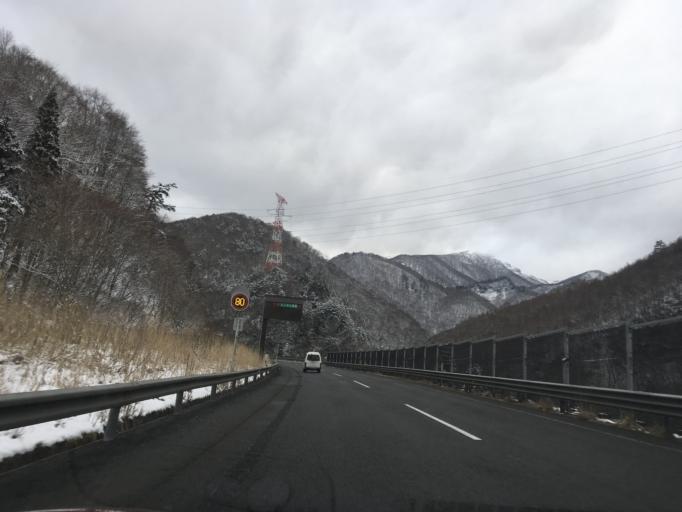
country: JP
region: Yamagata
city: Yamagata-shi
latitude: 38.2290
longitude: 140.4944
